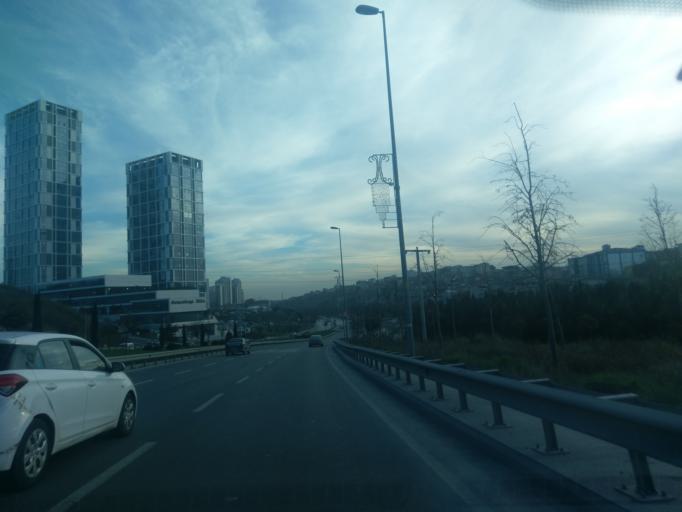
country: TR
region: Istanbul
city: Basaksehir
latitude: 41.0594
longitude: 28.7582
